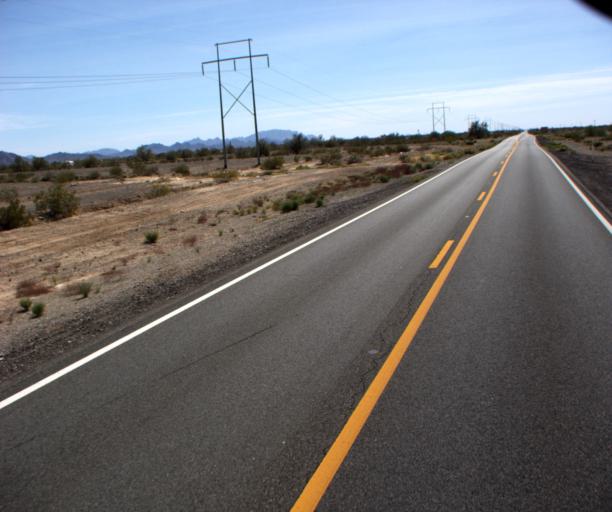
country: US
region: Arizona
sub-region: La Paz County
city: Quartzsite
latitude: 33.6296
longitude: -114.2171
